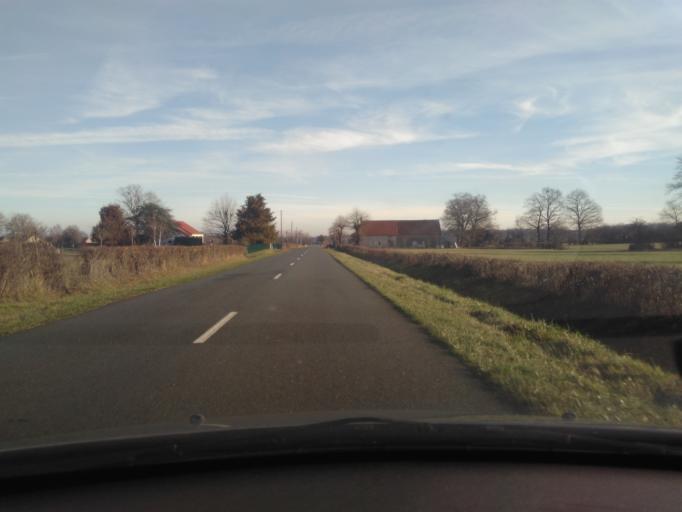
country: FR
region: Centre
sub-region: Departement du Cher
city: Le Chatelet
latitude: 46.6391
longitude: 2.2394
